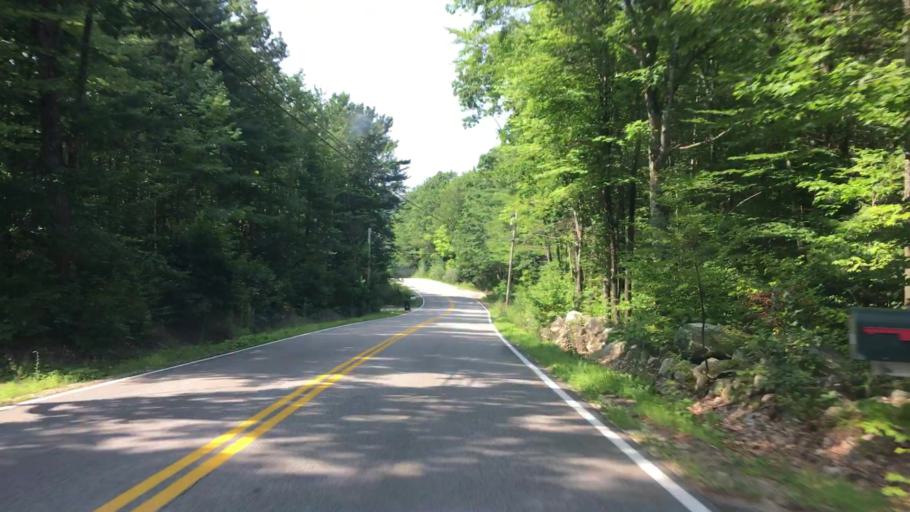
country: US
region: Maine
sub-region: Cumberland County
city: Raymond
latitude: 43.9607
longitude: -70.4170
